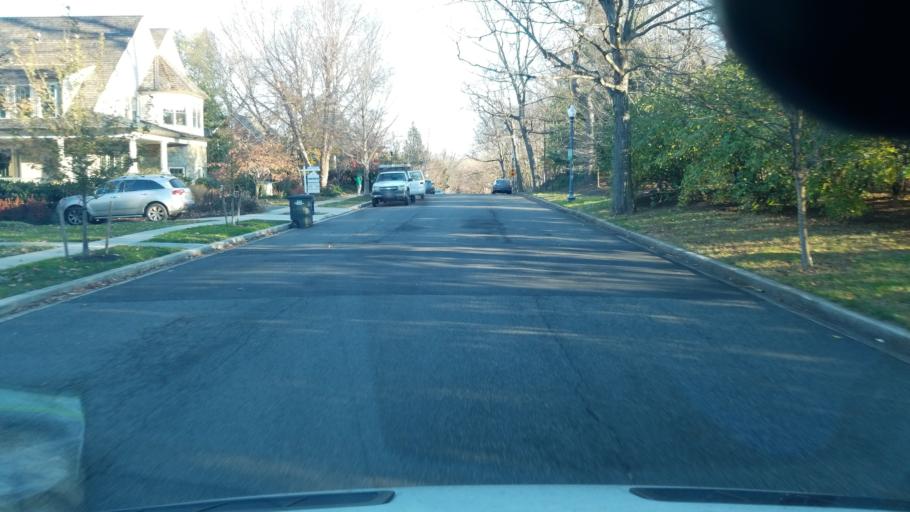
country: US
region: Maryland
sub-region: Montgomery County
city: Friendship Village
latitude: 38.9379
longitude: -77.0925
